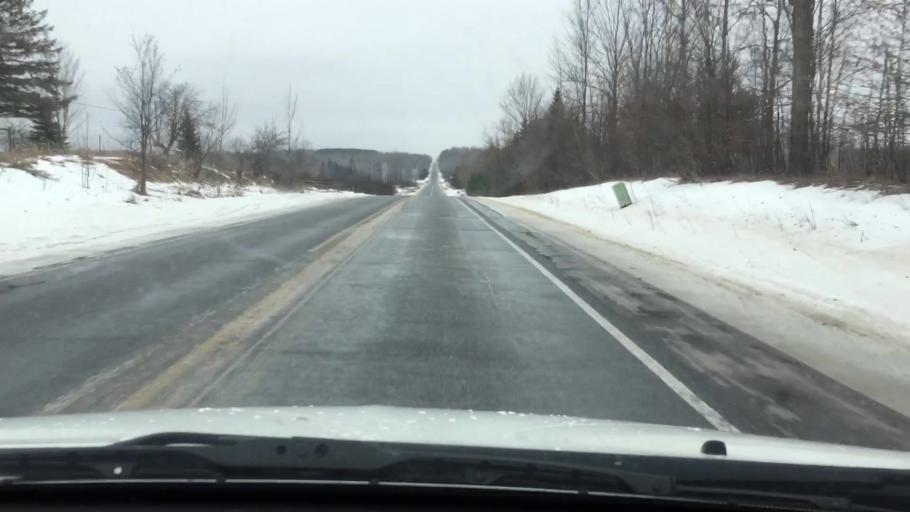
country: US
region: Michigan
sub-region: Wexford County
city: Cadillac
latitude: 44.1091
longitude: -85.4443
